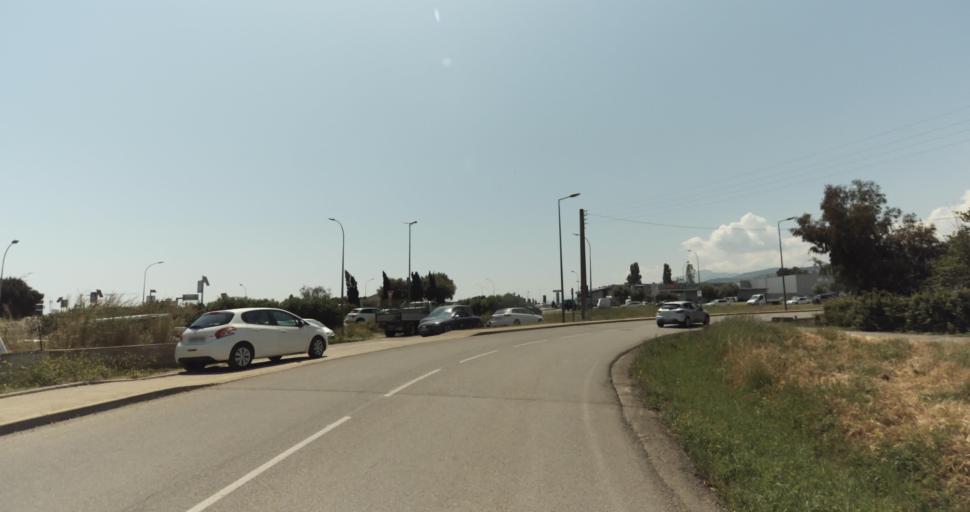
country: FR
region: Corsica
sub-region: Departement de la Haute-Corse
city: Biguglia
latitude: 42.5951
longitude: 9.4383
